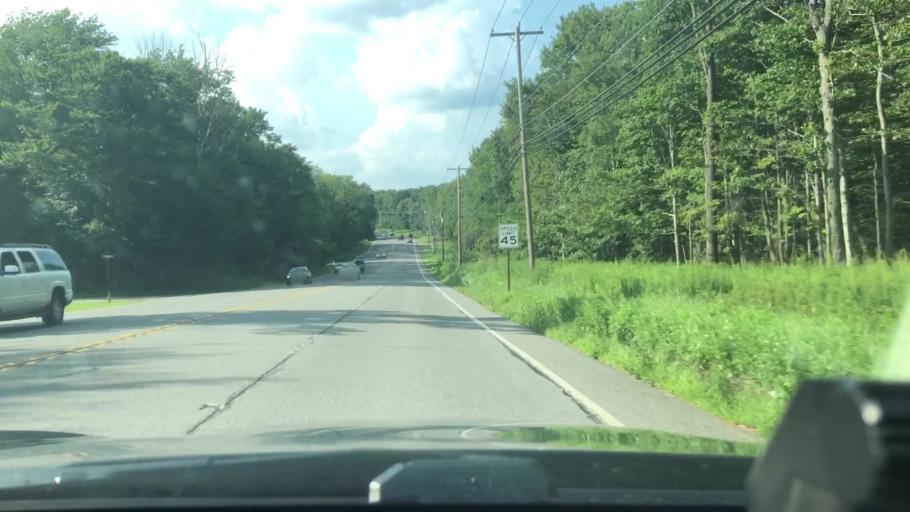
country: US
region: Pennsylvania
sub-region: Lackawanna County
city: Moscow
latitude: 41.2766
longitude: -75.5067
